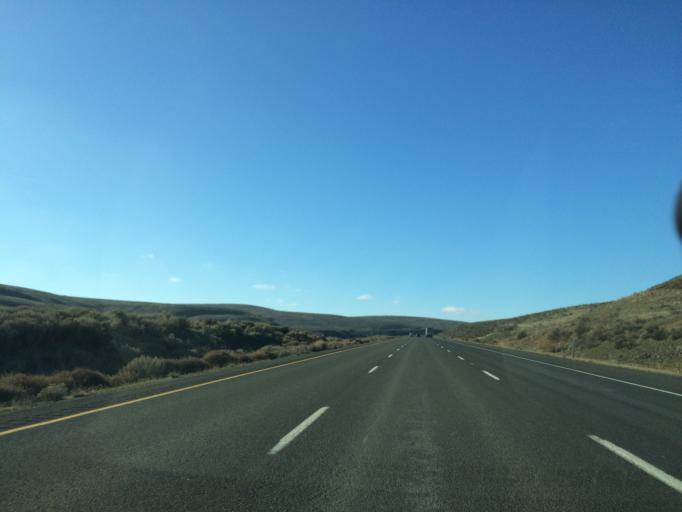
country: US
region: Washington
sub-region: Grant County
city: Mattawa
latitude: 46.9388
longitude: -120.0321
